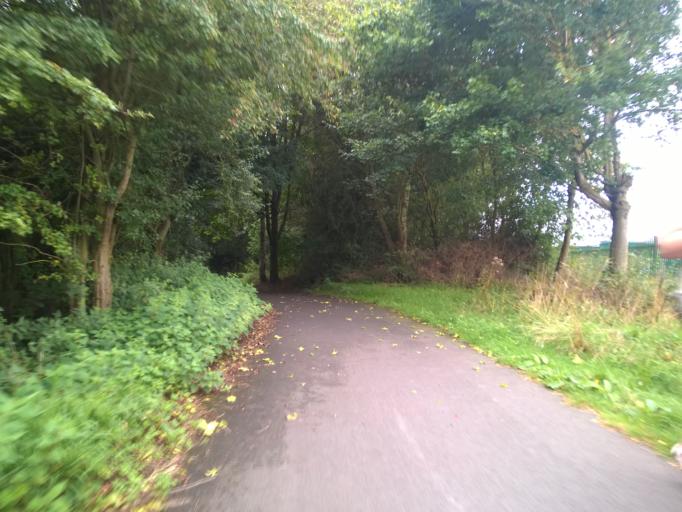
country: GB
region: England
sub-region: Leicestershire
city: Glenfield
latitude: 52.6489
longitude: -1.2149
